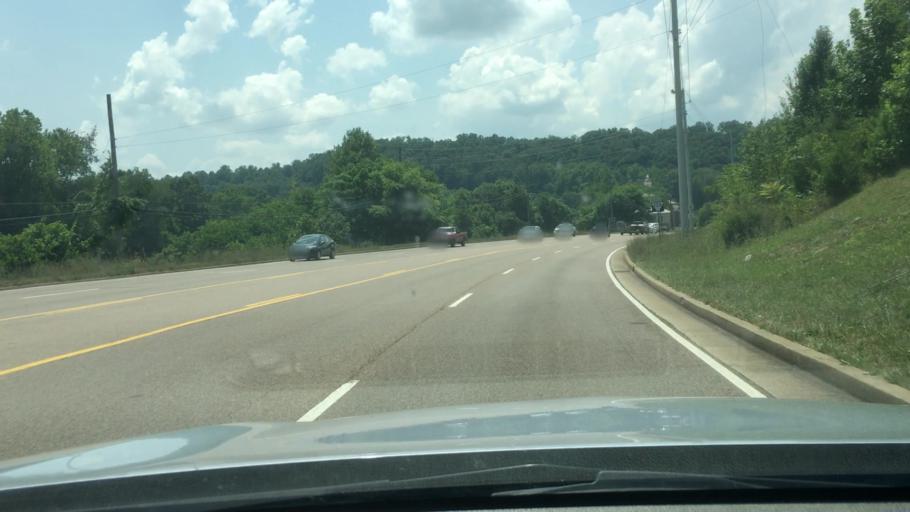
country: US
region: Tennessee
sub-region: Sullivan County
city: Blountville
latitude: 36.5366
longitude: -82.3281
